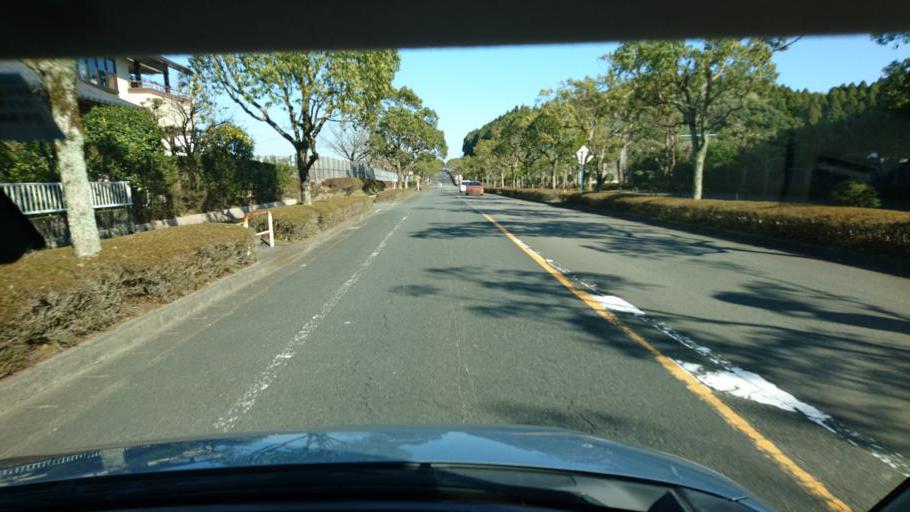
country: JP
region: Miyazaki
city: Miyazaki-shi
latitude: 31.8320
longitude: 131.4266
